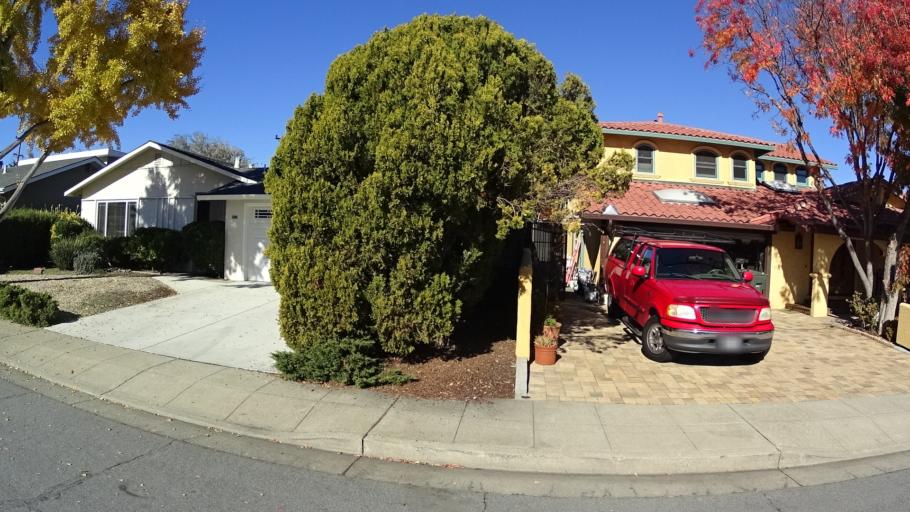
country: US
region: California
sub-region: Santa Clara County
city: Sunnyvale
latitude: 37.3611
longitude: -122.0124
